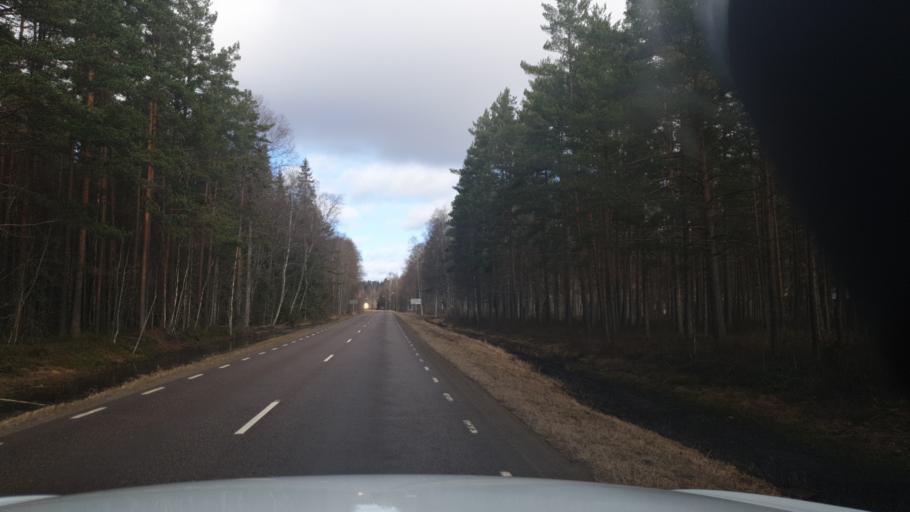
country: SE
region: Vaermland
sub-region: Arvika Kommun
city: Arvika
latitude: 59.6565
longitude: 12.8878
